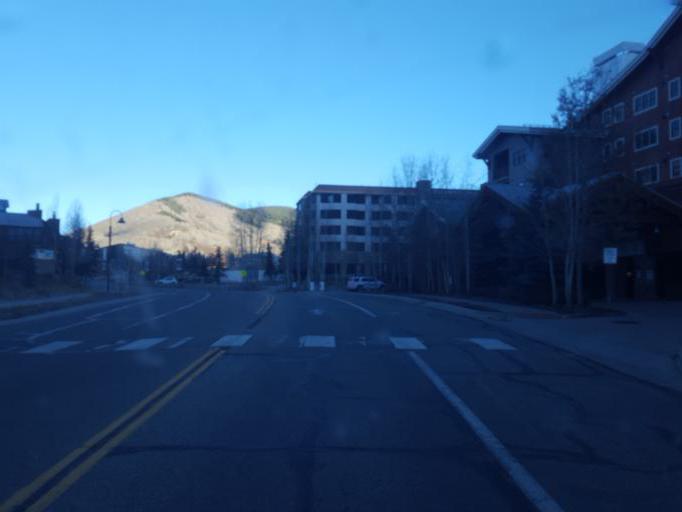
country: US
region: Colorado
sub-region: Gunnison County
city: Crested Butte
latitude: 38.8998
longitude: -106.9674
